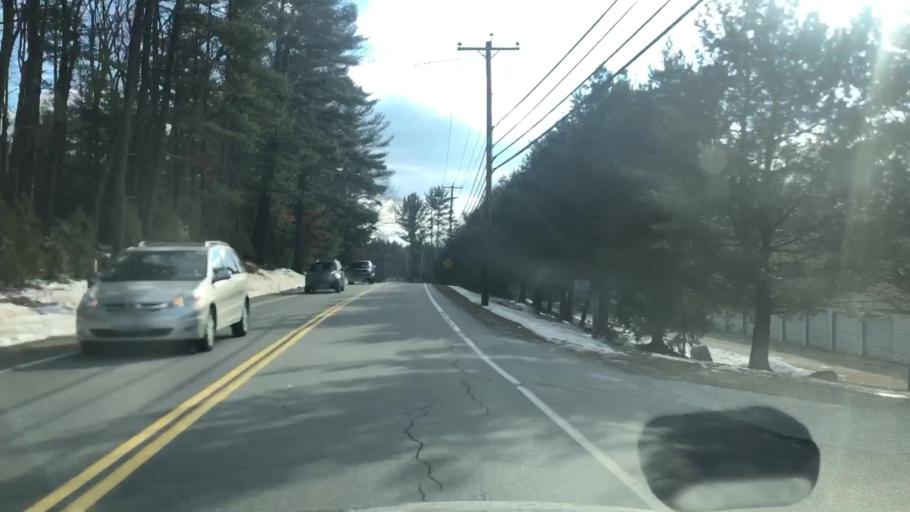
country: US
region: New Hampshire
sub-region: Hillsborough County
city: Milford
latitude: 42.8499
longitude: -71.6625
